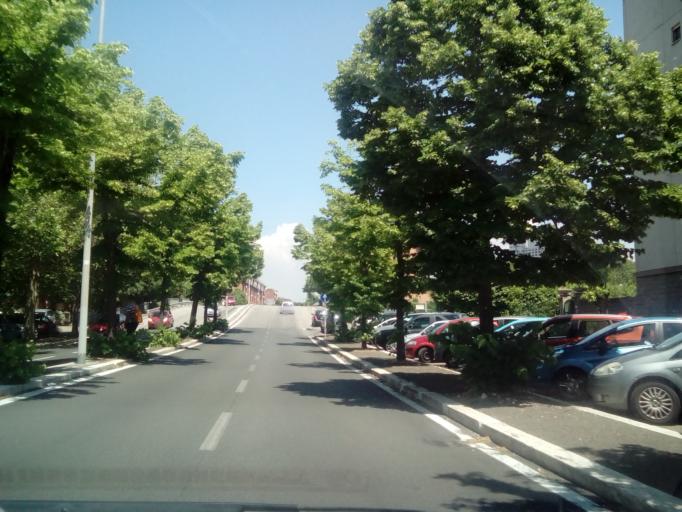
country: IT
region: Latium
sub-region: Citta metropolitana di Roma Capitale
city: Vitinia
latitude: 41.8171
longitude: 12.4485
